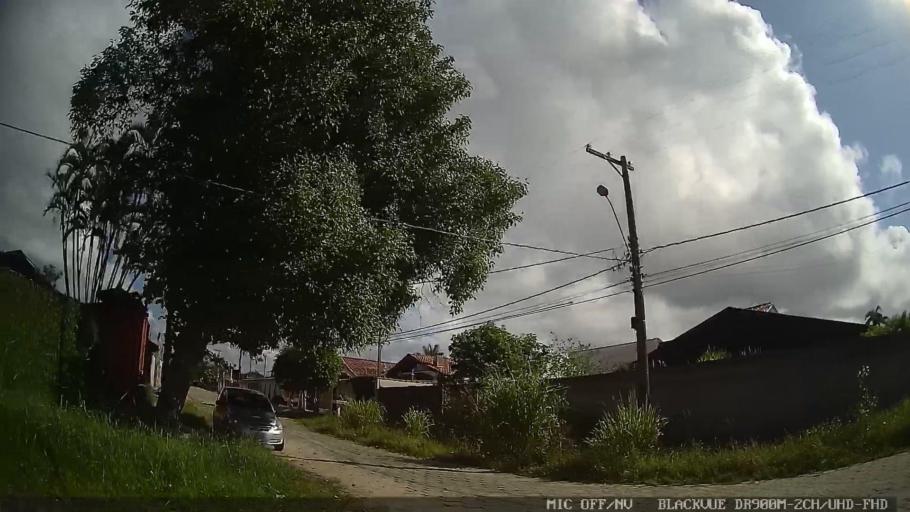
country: BR
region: Sao Paulo
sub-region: Peruibe
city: Peruibe
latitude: -24.2755
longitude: -46.9393
